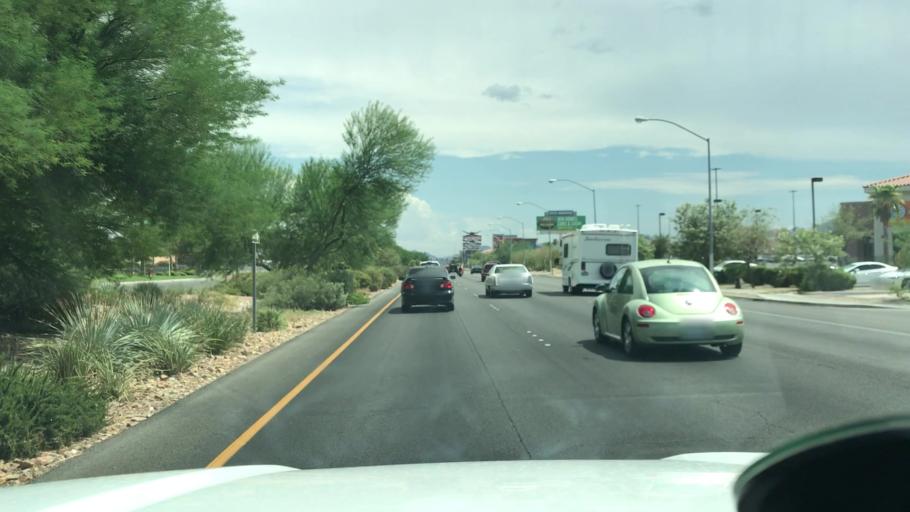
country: US
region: Nevada
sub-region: Clark County
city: Whitney
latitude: 36.1117
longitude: -115.0633
